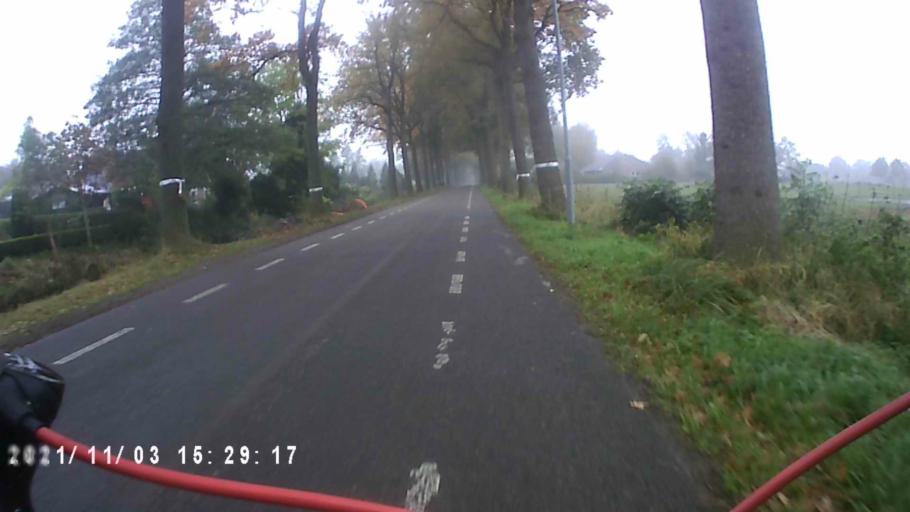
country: NL
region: Groningen
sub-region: Gemeente Leek
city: Leek
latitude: 53.1364
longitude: 6.3729
